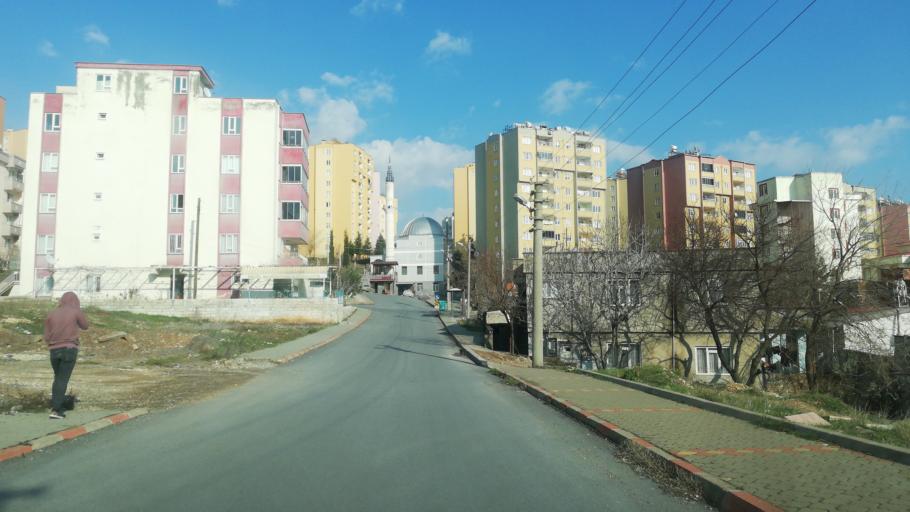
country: TR
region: Kahramanmaras
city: Kahramanmaras
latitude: 37.5941
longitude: 36.8992
